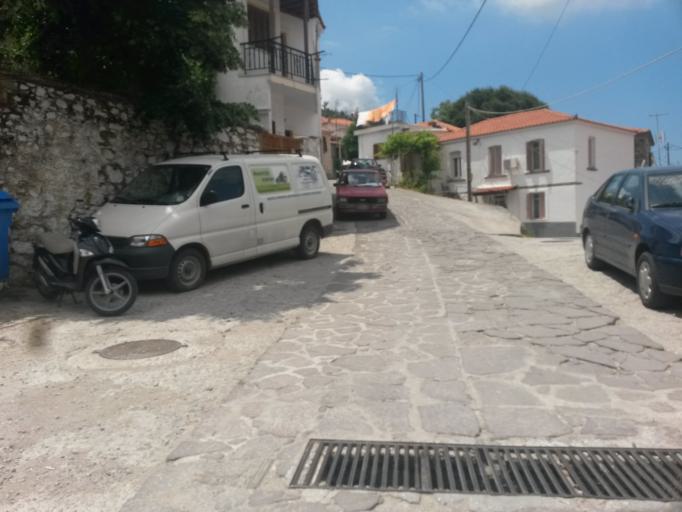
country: GR
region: North Aegean
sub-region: Nomos Lesvou
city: Petra
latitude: 39.2591
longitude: 26.0738
